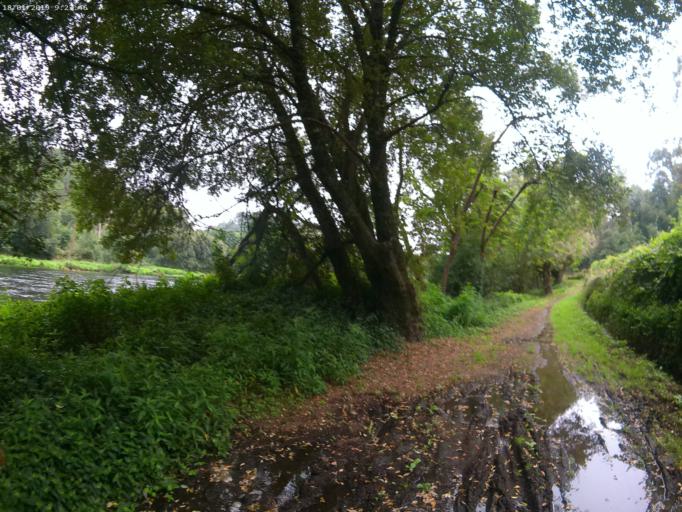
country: PT
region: Viana do Castelo
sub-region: Ponte da Barca
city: Ponte da Barca
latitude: 41.8032
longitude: -8.4635
